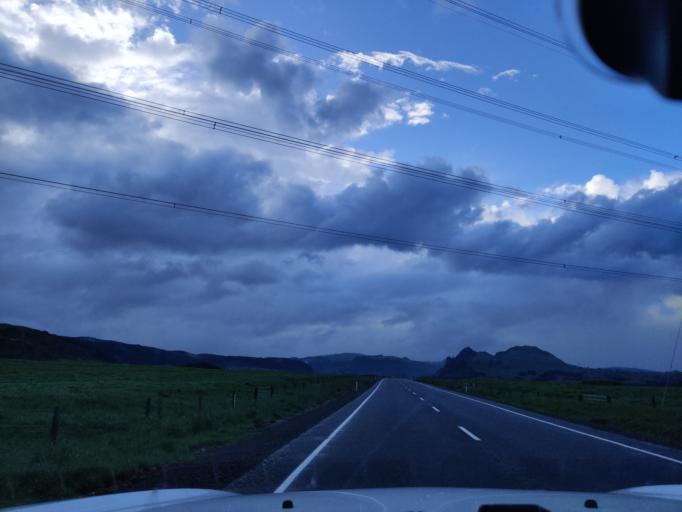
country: NZ
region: Waikato
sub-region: South Waikato District
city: Tokoroa
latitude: -38.3976
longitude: 175.7870
